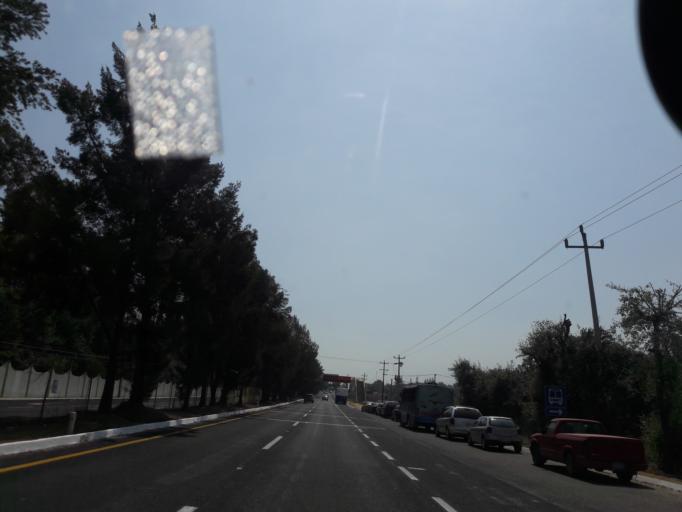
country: MX
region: Tlaxcala
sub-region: Panotla
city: Fraccionamiento la Virgen
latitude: 19.3228
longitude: -98.2800
